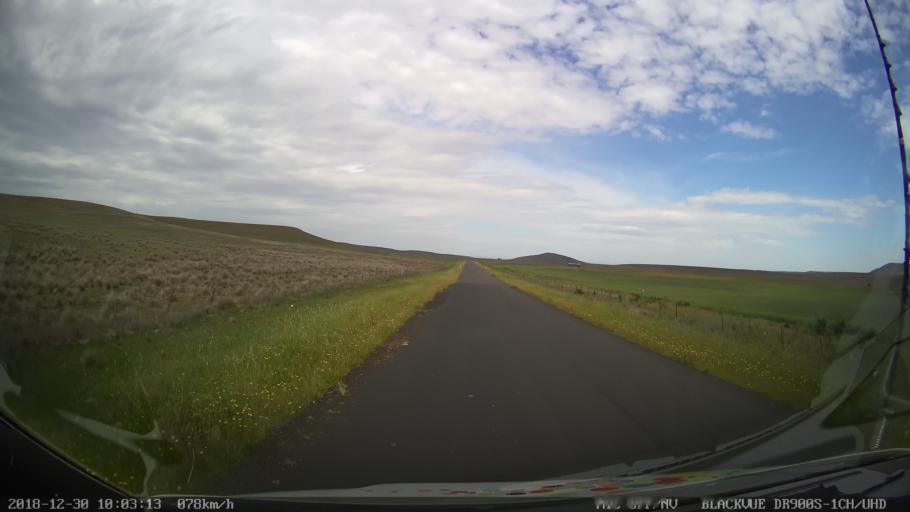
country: AU
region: New South Wales
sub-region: Cooma-Monaro
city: Cooma
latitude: -36.5152
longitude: 149.1608
